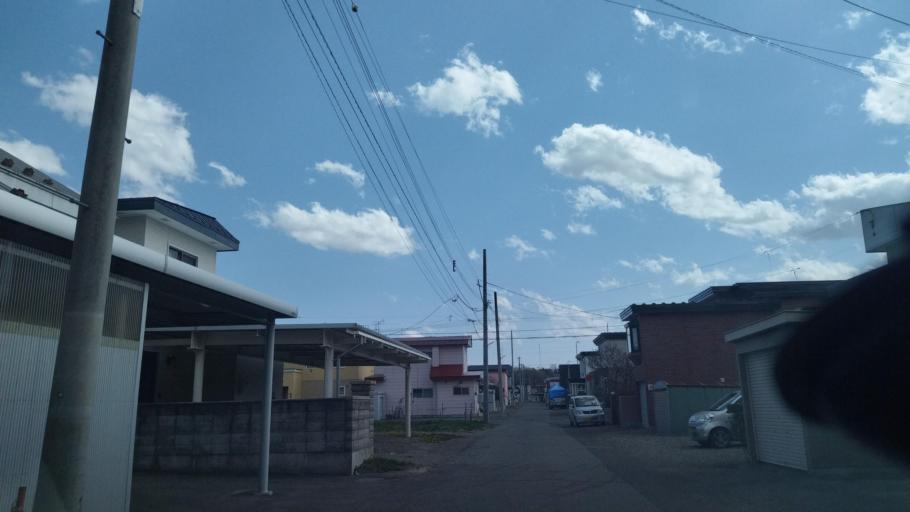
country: JP
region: Hokkaido
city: Obihiro
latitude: 42.9082
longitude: 143.1574
